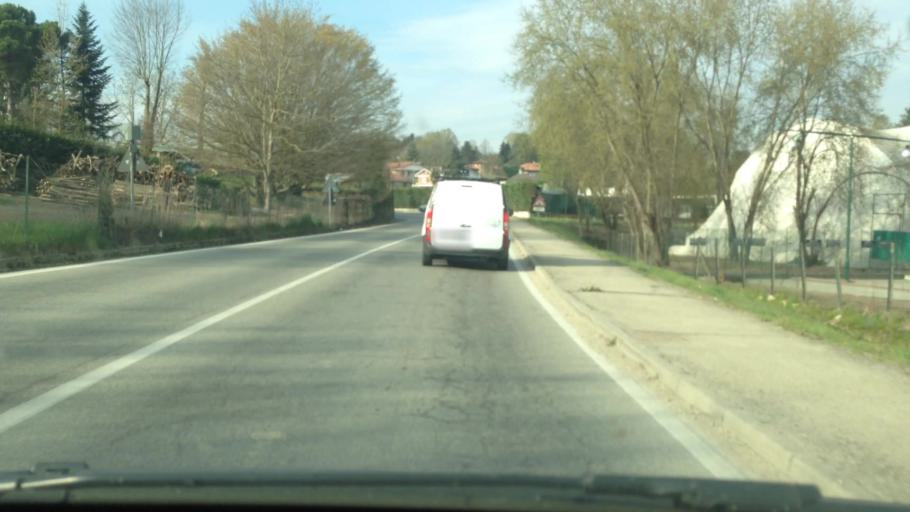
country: IT
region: Piedmont
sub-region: Provincia di Asti
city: San Damiano d'Asti
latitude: 44.8335
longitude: 8.0613
